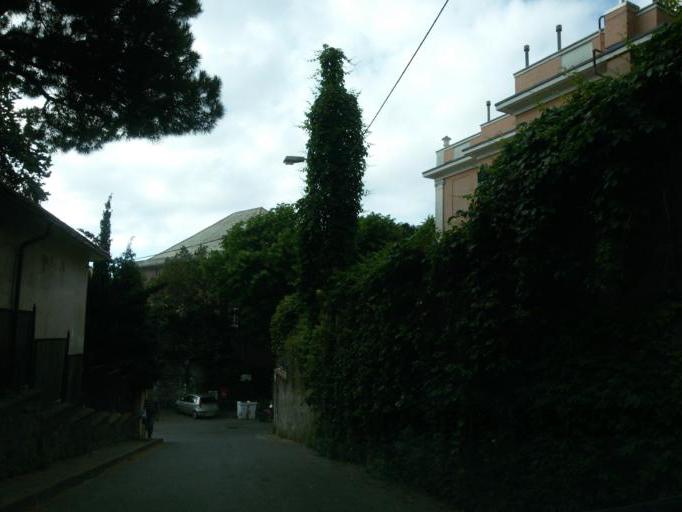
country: IT
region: Liguria
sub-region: Provincia di Genova
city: Genoa
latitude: 44.4024
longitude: 8.9603
